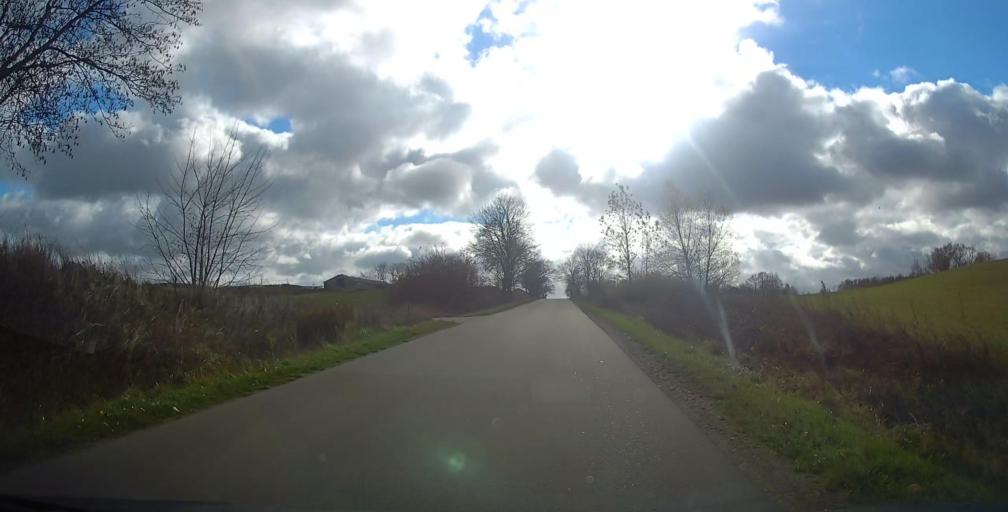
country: PL
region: Podlasie
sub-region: Suwalki
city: Suwalki
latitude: 54.3205
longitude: 22.8631
